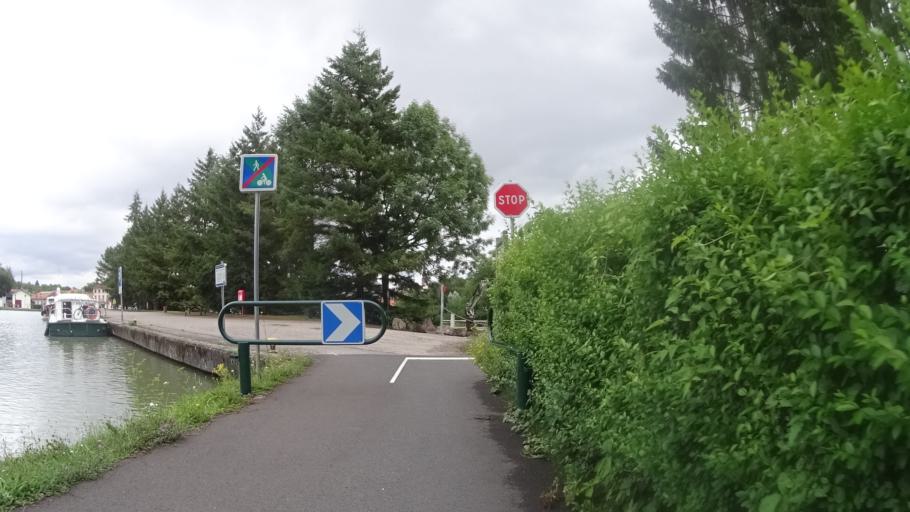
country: FR
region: Lorraine
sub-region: Departement de Meurthe-et-Moselle
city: Einville-au-Jard
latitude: 48.6536
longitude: 6.4812
